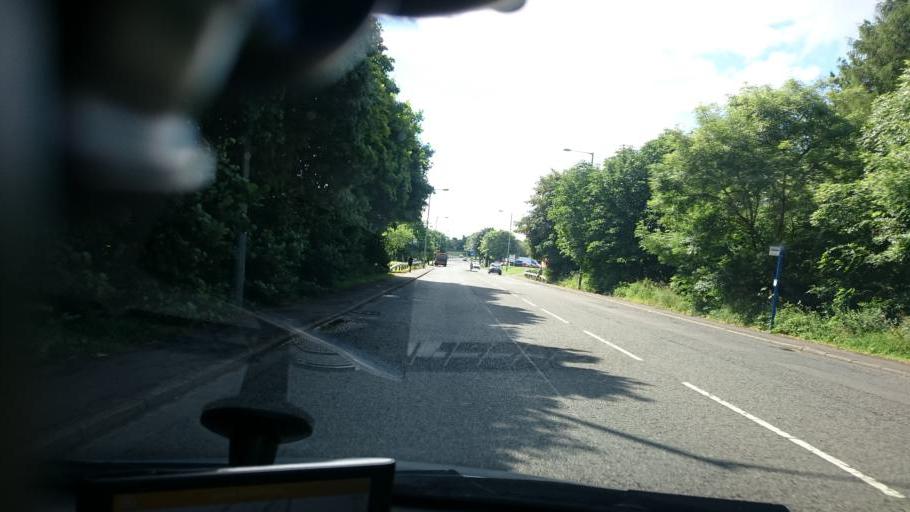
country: GB
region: Scotland
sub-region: Falkirk
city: Dunipace
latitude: 56.0158
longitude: -3.9174
